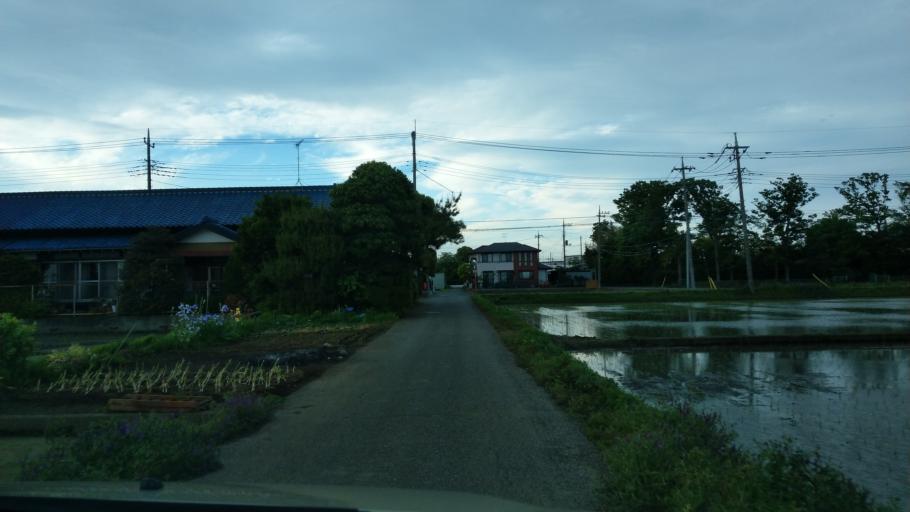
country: JP
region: Saitama
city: Yono
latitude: 35.8821
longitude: 139.5929
